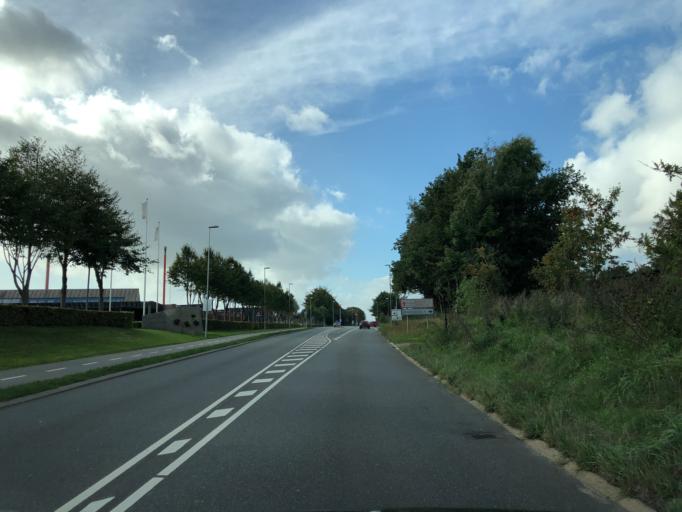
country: DK
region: Central Jutland
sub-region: Holstebro Kommune
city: Holstebro
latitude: 56.3661
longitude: 8.5822
